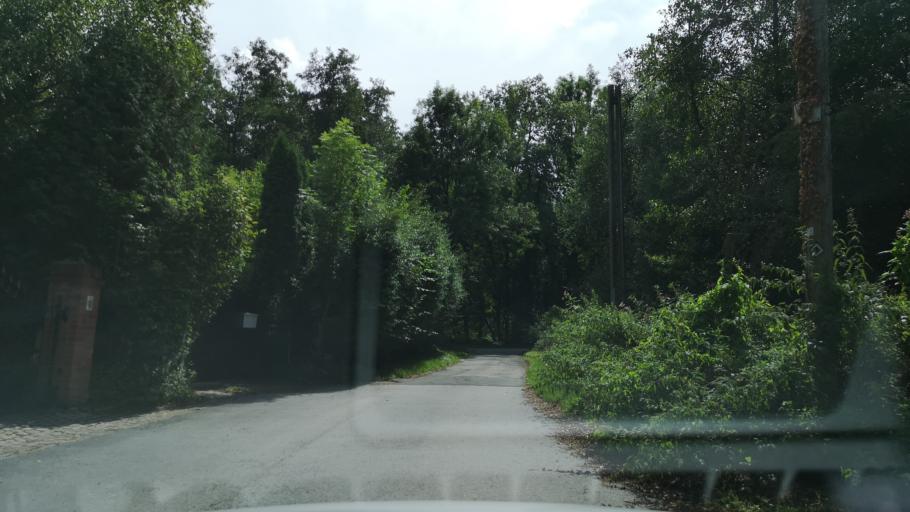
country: DE
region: North Rhine-Westphalia
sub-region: Regierungsbezirk Dusseldorf
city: Heiligenhaus
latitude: 51.3601
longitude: 6.9918
